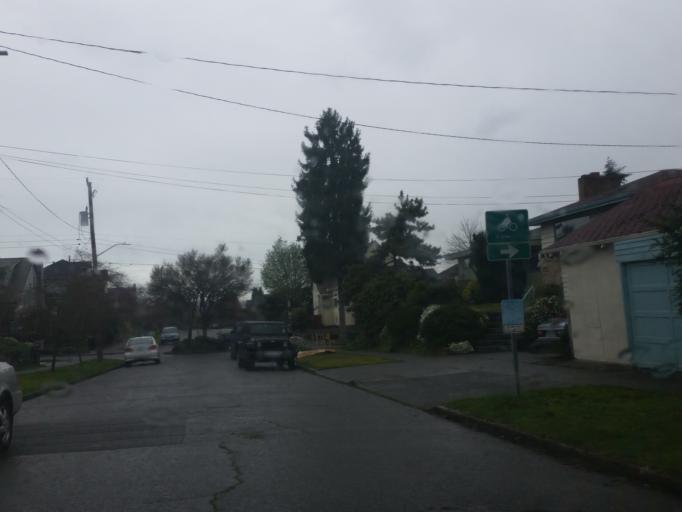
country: US
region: Washington
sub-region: King County
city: Seattle
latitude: 47.6719
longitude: -122.3514
